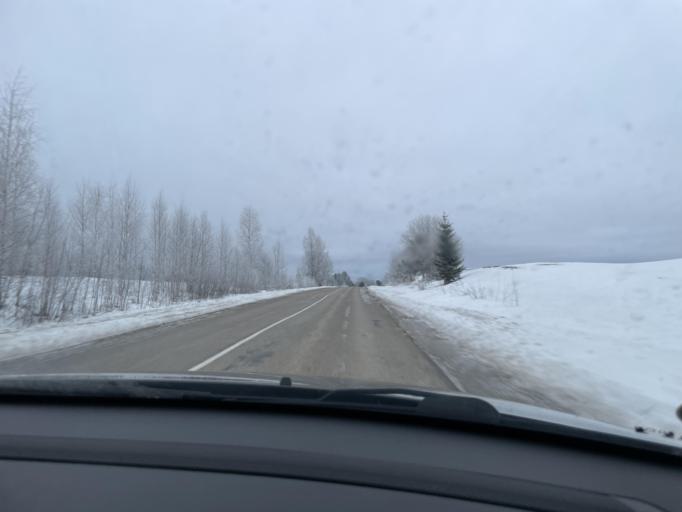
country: LV
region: Rezekne
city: Rezekne
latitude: 56.4382
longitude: 27.5212
